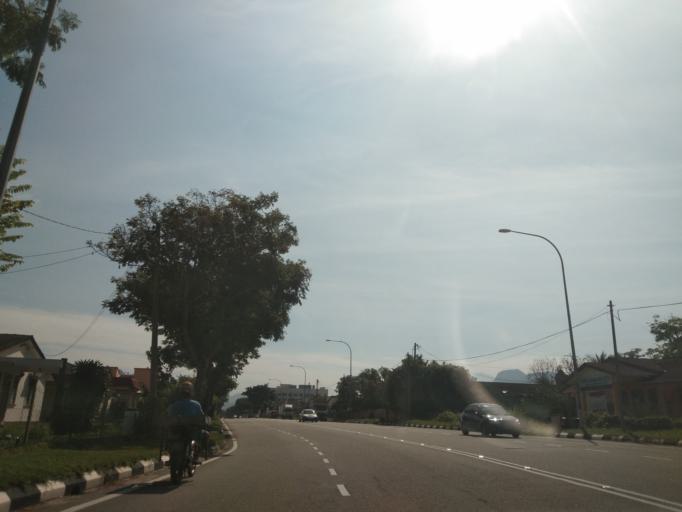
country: MY
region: Perak
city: Ipoh
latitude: 4.5687
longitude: 101.1241
